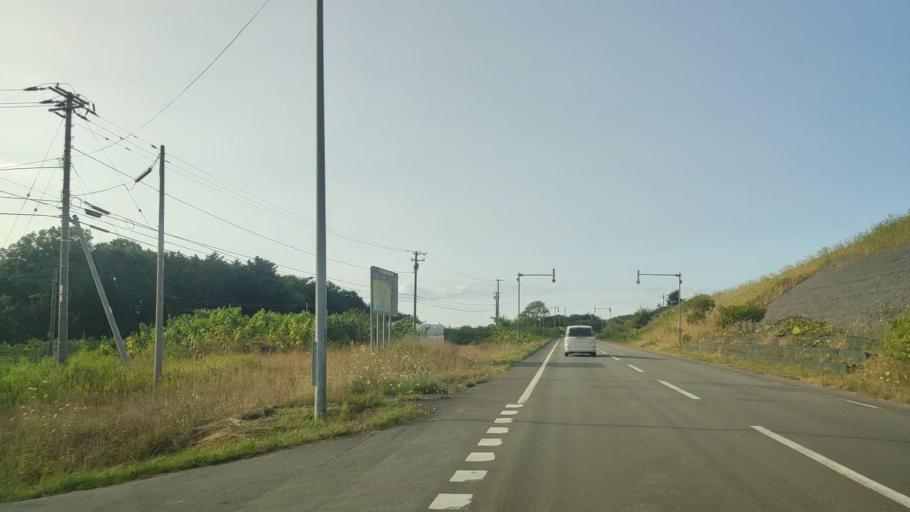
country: JP
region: Hokkaido
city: Makubetsu
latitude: 45.0559
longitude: 141.7491
